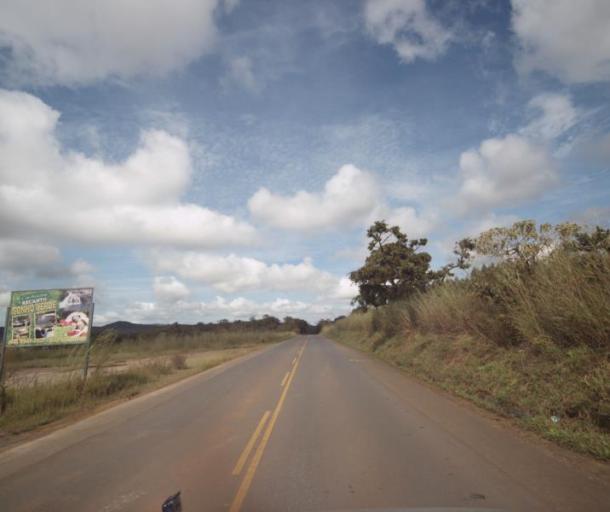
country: BR
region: Goias
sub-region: Pirenopolis
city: Pirenopolis
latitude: -15.8605
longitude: -48.7702
